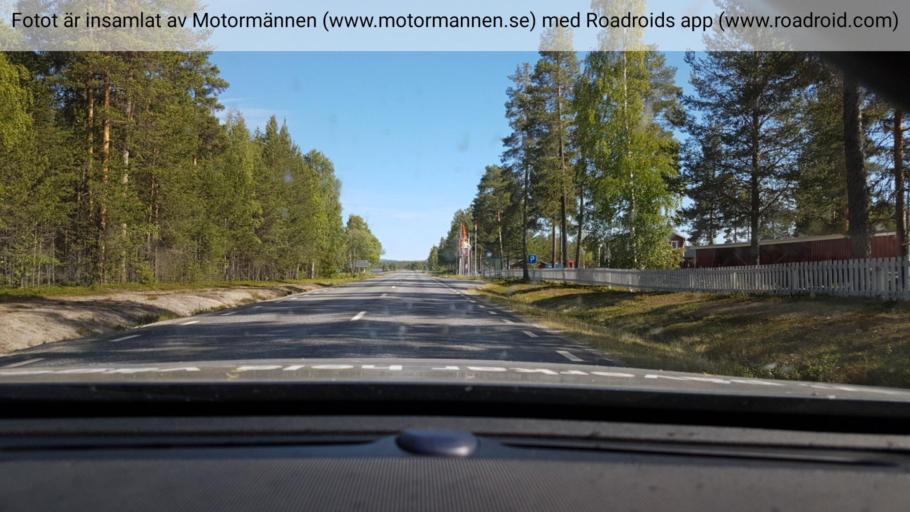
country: SE
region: Vaesterbotten
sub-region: Lycksele Kommun
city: Soderfors
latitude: 64.7596
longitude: 18.1646
